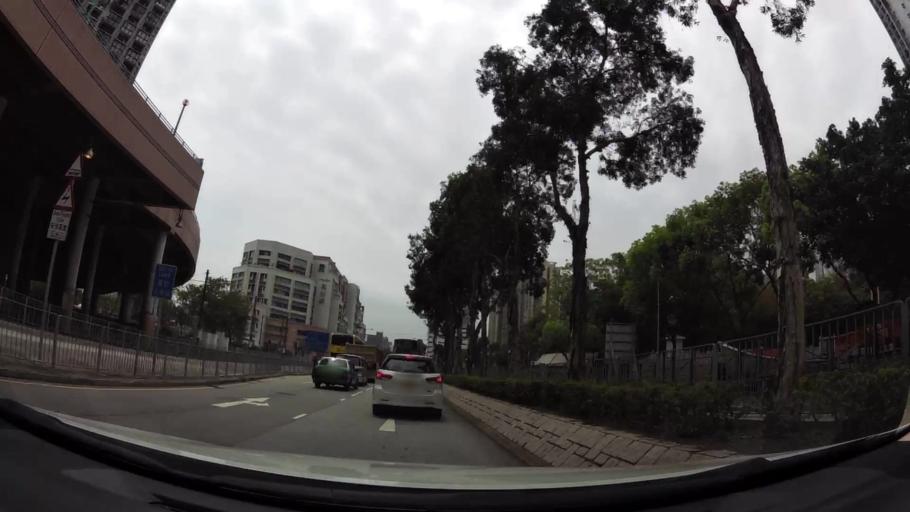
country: HK
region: Tuen Mun
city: Tuen Mun
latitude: 22.3827
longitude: 113.9761
